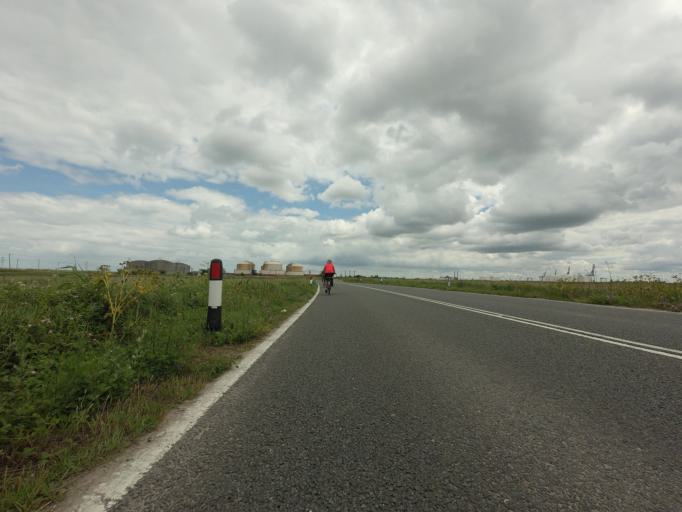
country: GB
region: England
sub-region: Medway
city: Allhallows
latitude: 51.4492
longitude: 0.6645
